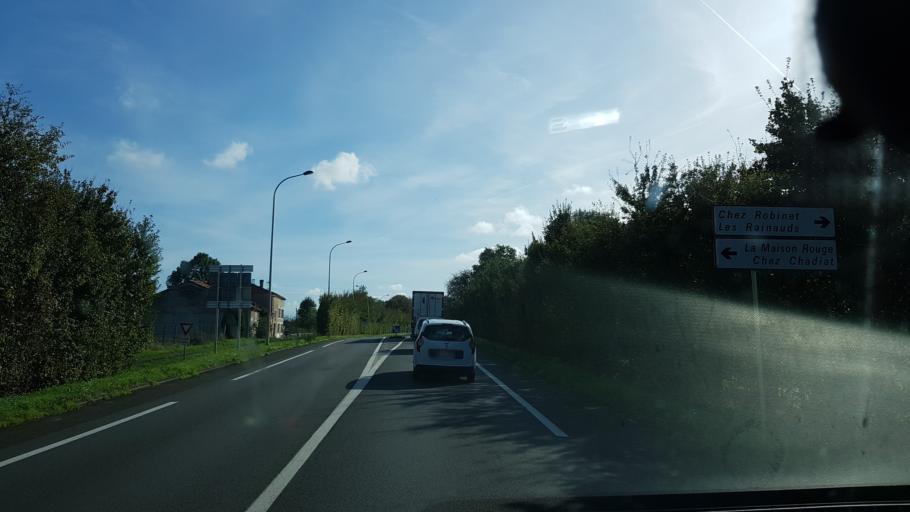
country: FR
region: Poitou-Charentes
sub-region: Departement de la Charente
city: Saint-Claud
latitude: 45.8836
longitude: 0.4694
